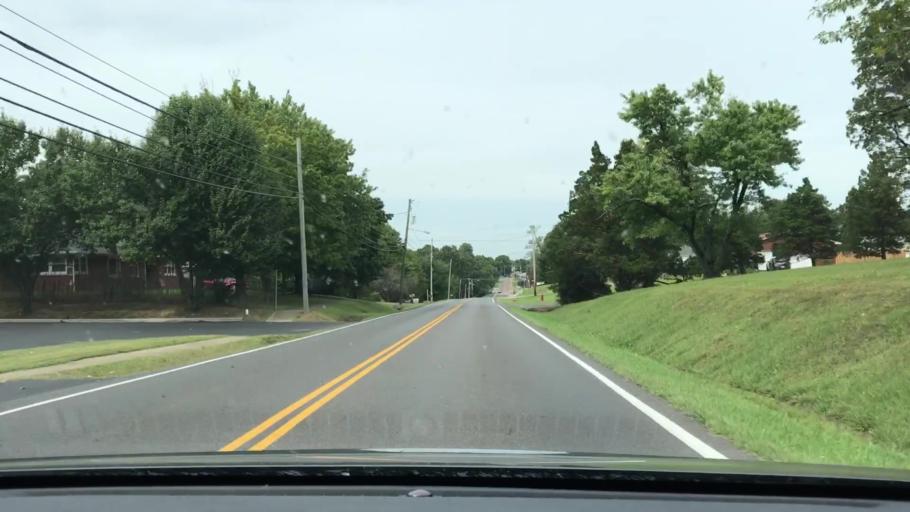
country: US
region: Kentucky
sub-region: Marshall County
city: Benton
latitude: 36.8478
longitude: -88.3500
